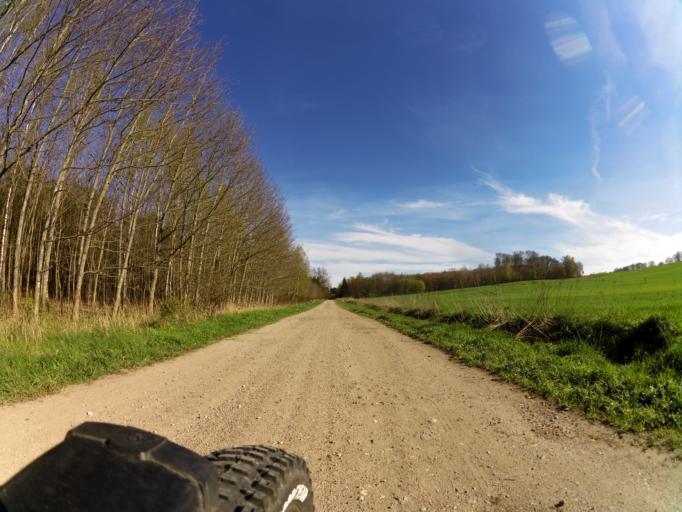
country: PL
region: West Pomeranian Voivodeship
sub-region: Powiat lobeski
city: Lobez
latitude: 53.7754
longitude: 15.5783
